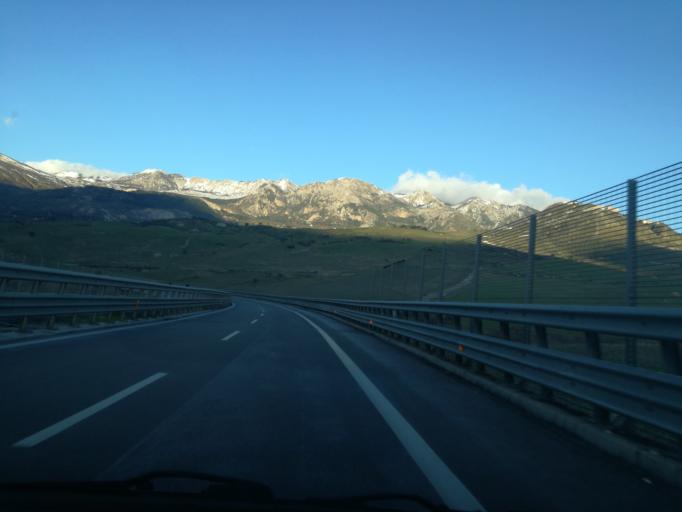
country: IT
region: Sicily
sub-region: Palermo
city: Polizzi Generosa
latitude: 37.8068
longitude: 13.9710
